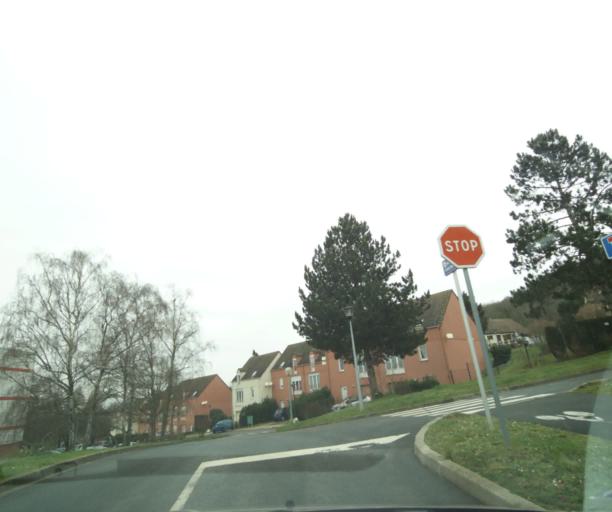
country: FR
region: Picardie
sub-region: Departement de l'Oise
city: Noyon
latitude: 49.5829
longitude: 3.0223
